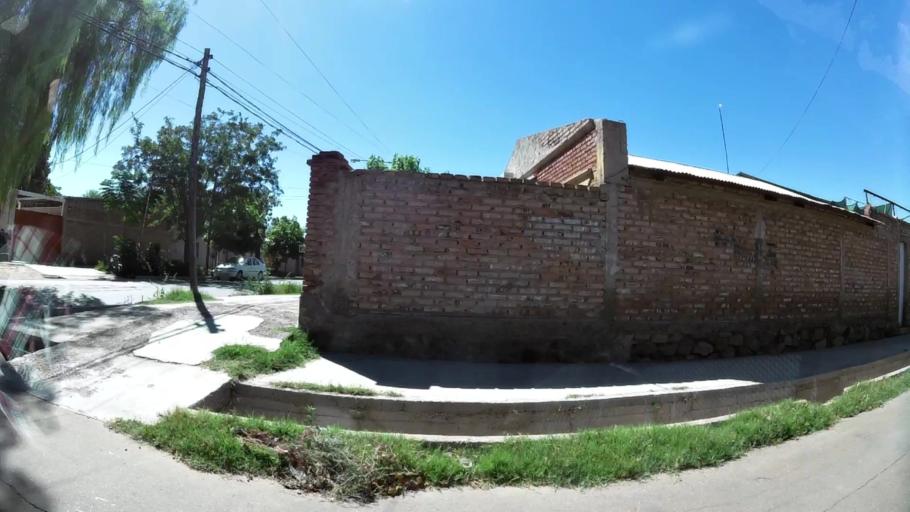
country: AR
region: Mendoza
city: Las Heras
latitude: -32.8333
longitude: -68.8375
